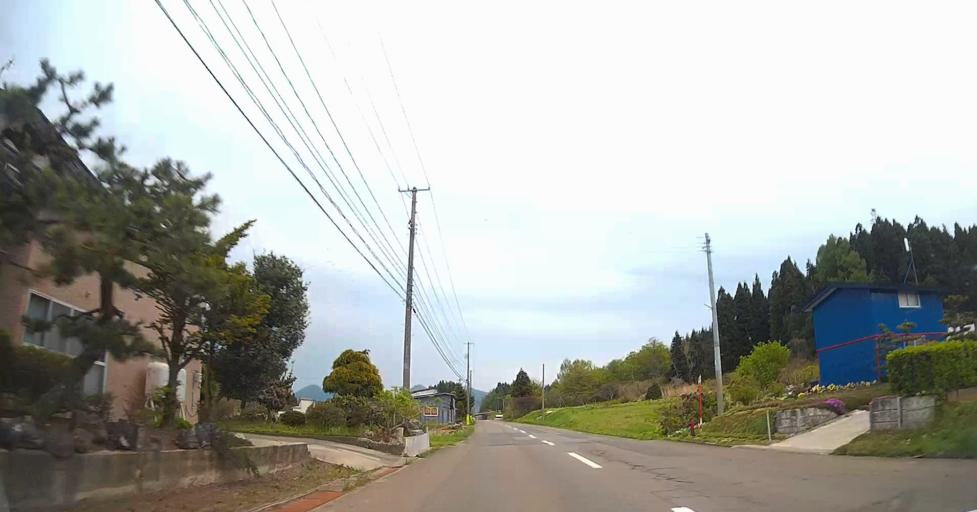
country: JP
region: Aomori
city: Shimokizukuri
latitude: 41.1791
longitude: 140.4661
